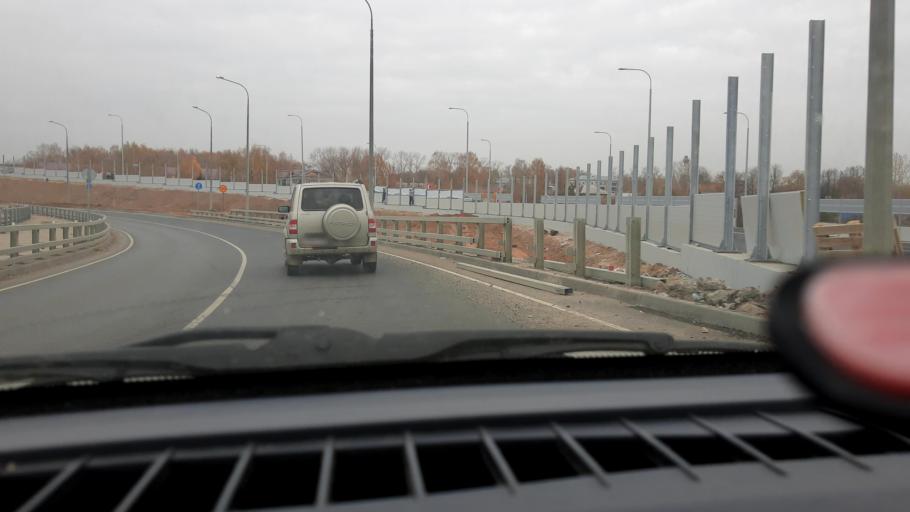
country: RU
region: Nizjnij Novgorod
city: Neklyudovo
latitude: 56.3994
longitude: 43.9906
